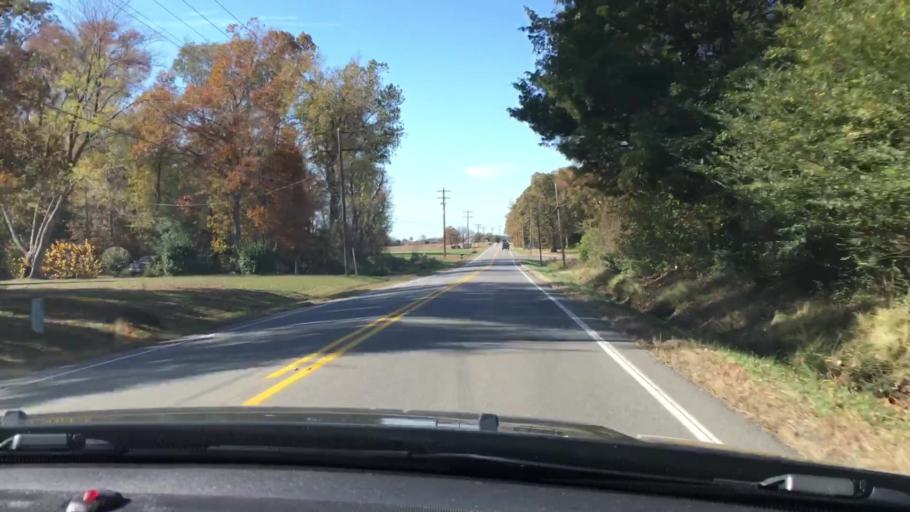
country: US
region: Virginia
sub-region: King William County
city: Central Garage
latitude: 37.7208
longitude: -77.0813
